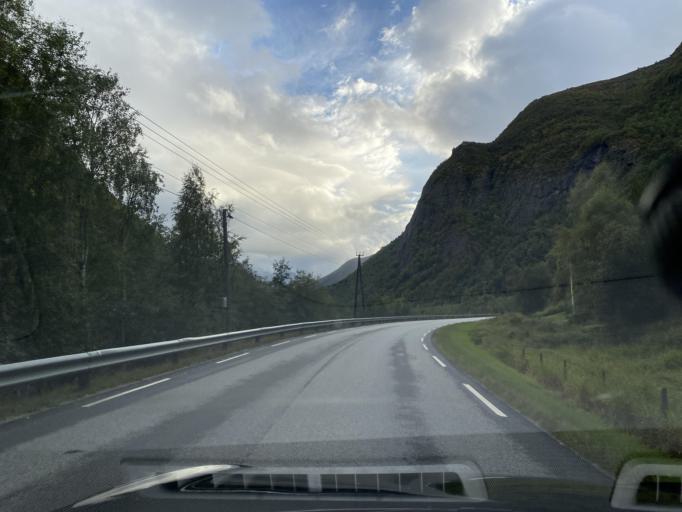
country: NO
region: Oppland
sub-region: Lom
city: Fossbergom
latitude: 61.7829
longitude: 8.4377
